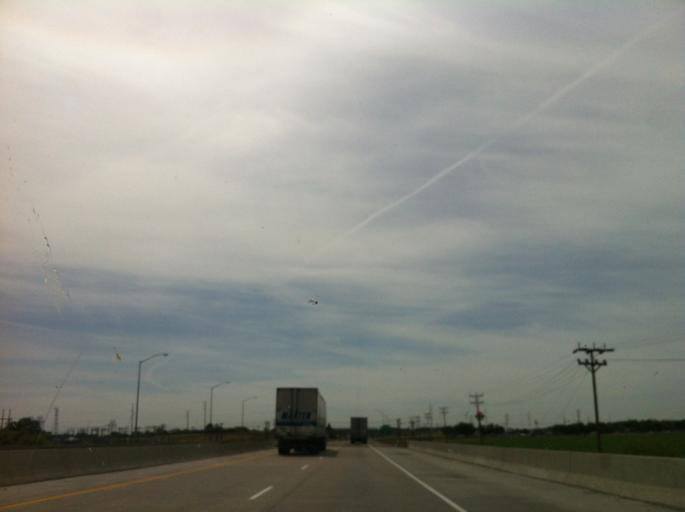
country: US
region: Oregon
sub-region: Malheur County
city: Ontario
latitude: 44.0543
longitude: -116.9839
